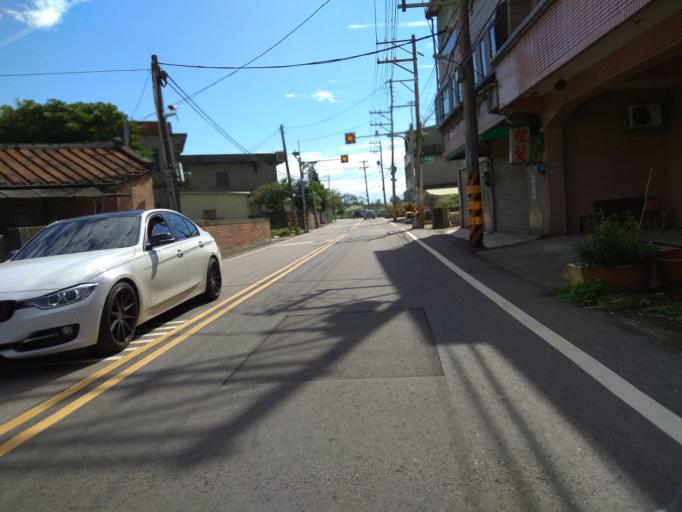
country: TW
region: Taiwan
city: Taoyuan City
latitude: 25.0445
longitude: 121.1214
